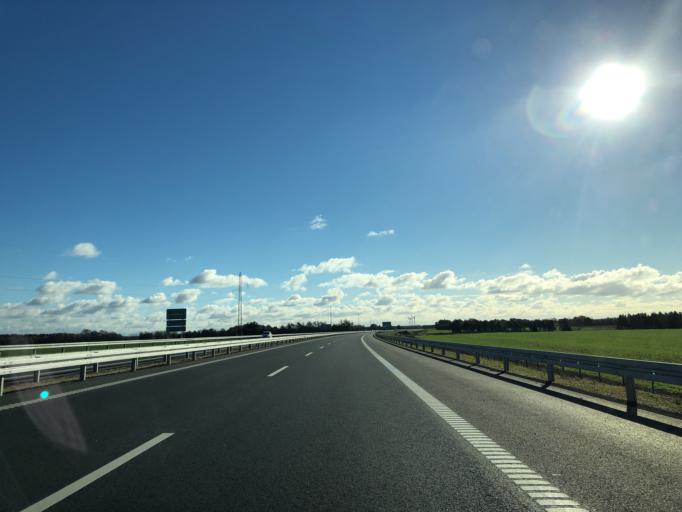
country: DK
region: Central Jutland
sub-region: Holstebro Kommune
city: Holstebro
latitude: 56.3634
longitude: 8.7274
